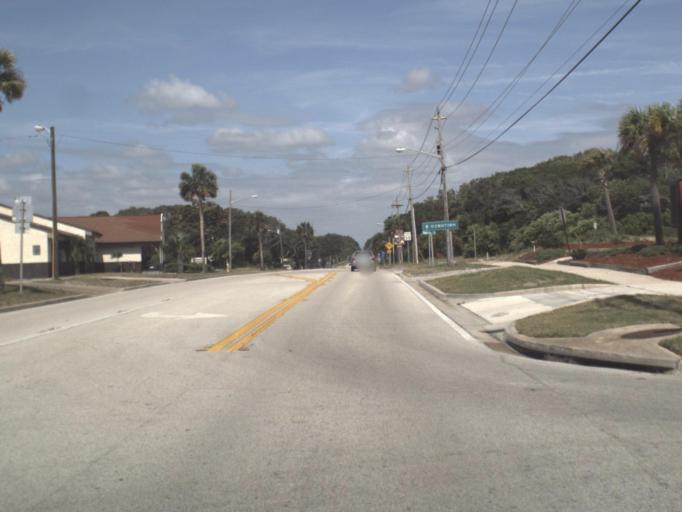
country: US
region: Florida
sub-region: Nassau County
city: Fernandina Beach
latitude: 30.6678
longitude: -81.4325
